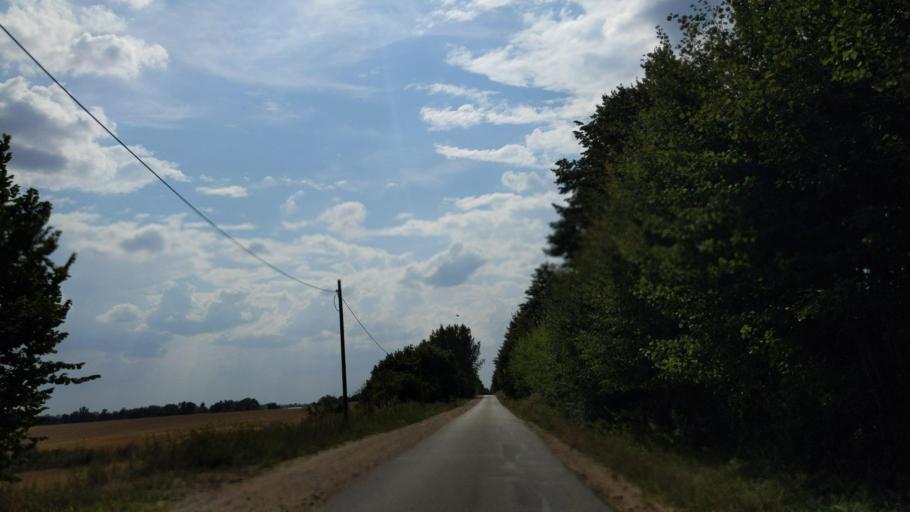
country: DE
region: Mecklenburg-Vorpommern
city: Selmsdorf
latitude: 53.8471
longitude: 10.9056
